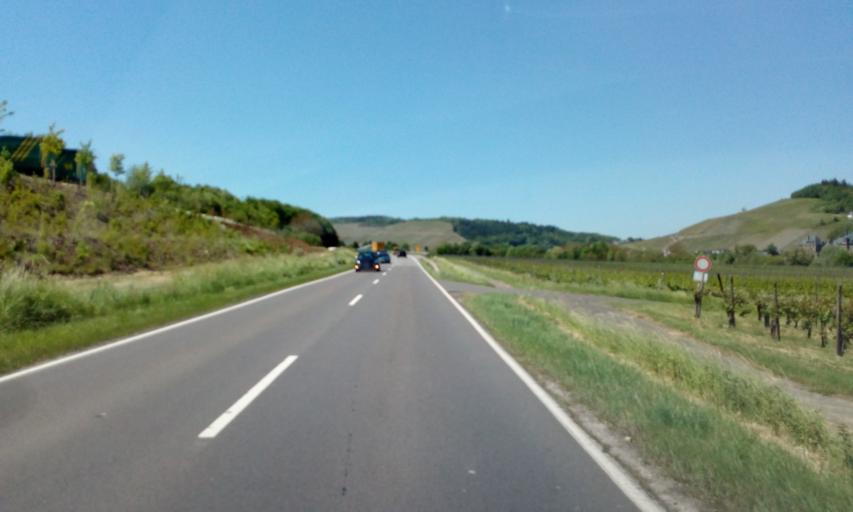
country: DE
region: Rheinland-Pfalz
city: Lieser
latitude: 49.9126
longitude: 7.0273
